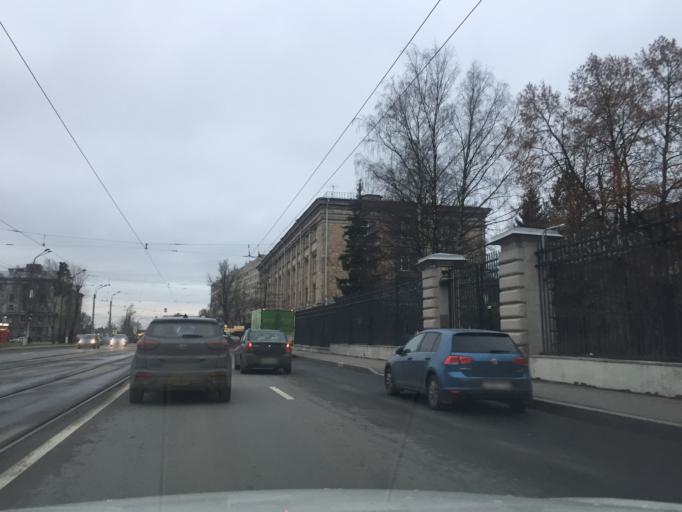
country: RU
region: St.-Petersburg
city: Kushelevka
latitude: 60.0030
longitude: 30.3670
